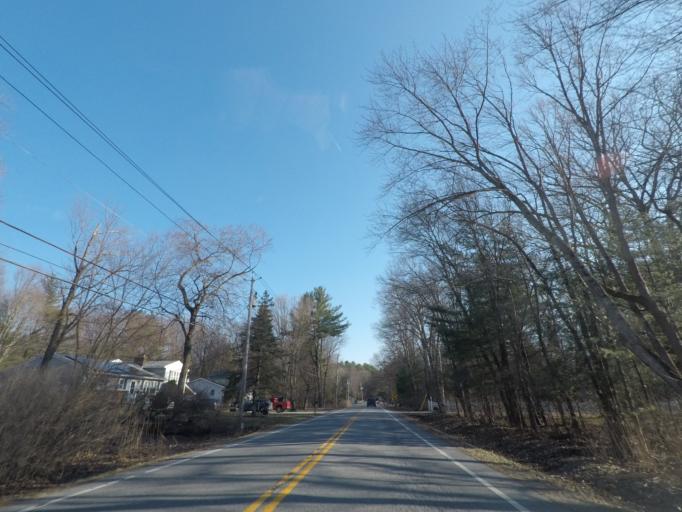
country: US
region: New York
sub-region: Saratoga County
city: Country Knolls
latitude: 42.8344
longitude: -73.7760
